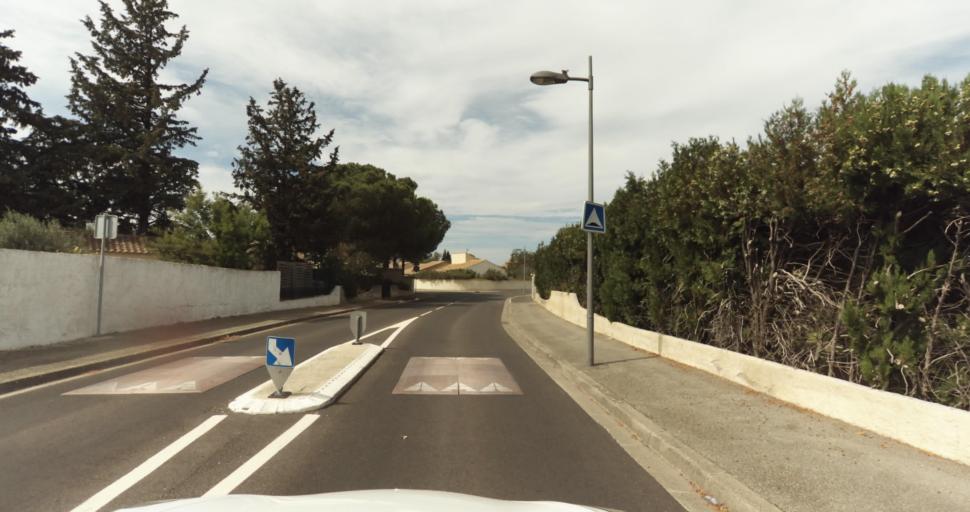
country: FR
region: Provence-Alpes-Cote d'Azur
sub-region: Departement des Bouches-du-Rhone
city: Miramas
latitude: 43.5762
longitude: 4.9933
